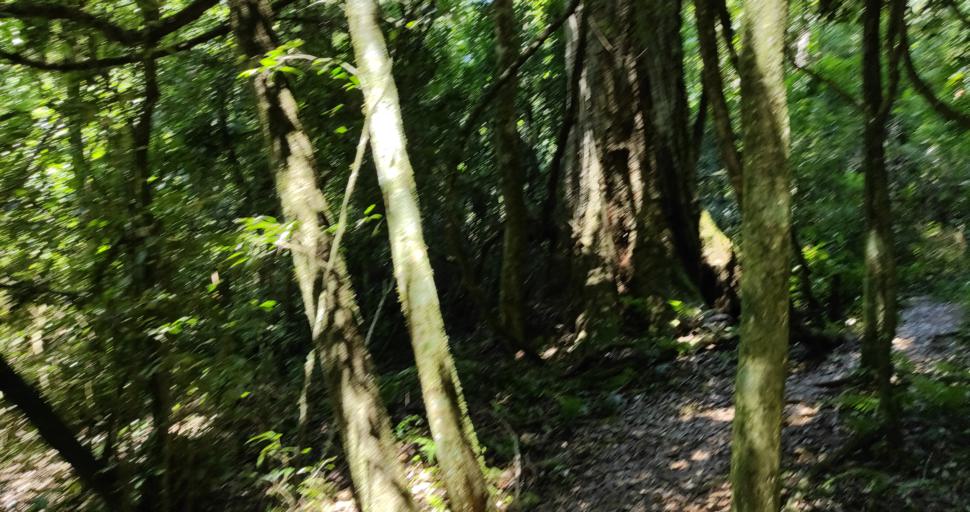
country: BR
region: Rio Grande do Sul
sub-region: Tres Passos
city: Tres Passos
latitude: -27.1487
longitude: -53.8979
